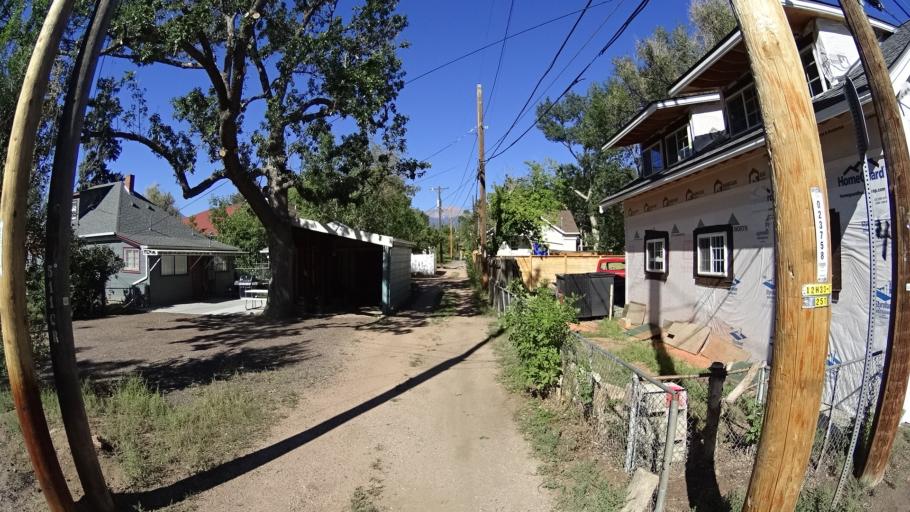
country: US
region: Colorado
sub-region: El Paso County
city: Colorado Springs
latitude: 38.8397
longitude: -104.8153
